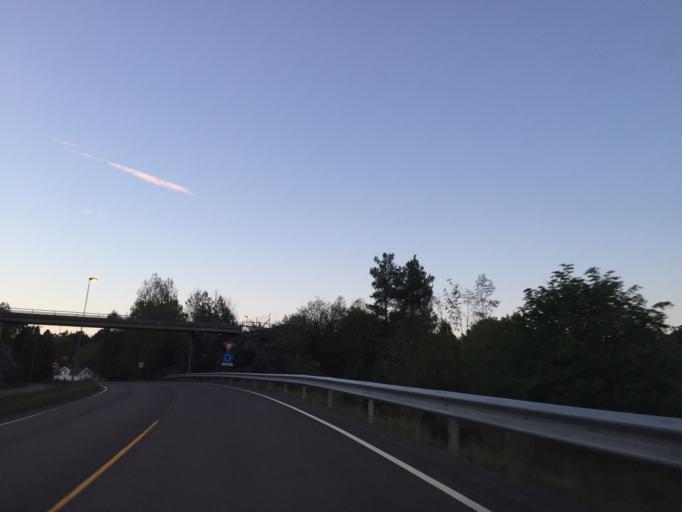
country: NO
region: Ostfold
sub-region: Moss
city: Moss
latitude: 59.5193
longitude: 10.6960
